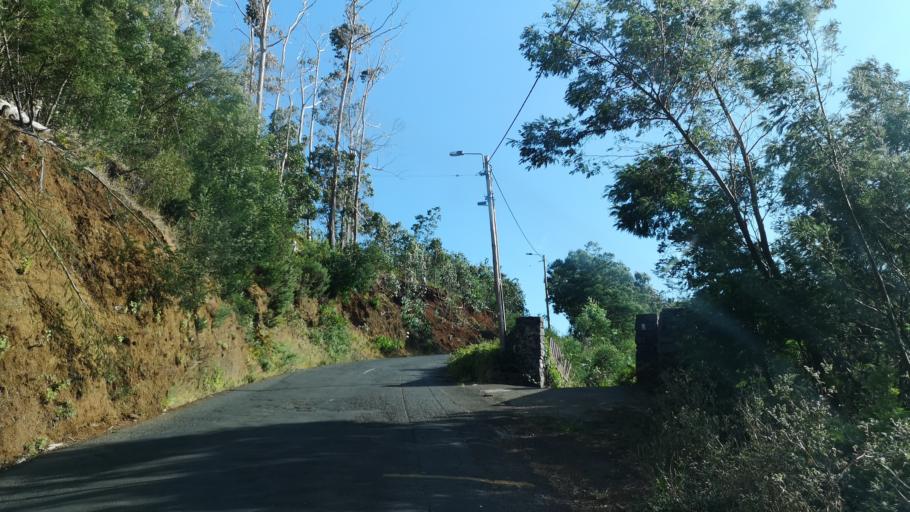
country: PT
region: Madeira
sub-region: Santa Cruz
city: Camacha
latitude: 32.6685
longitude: -16.8387
